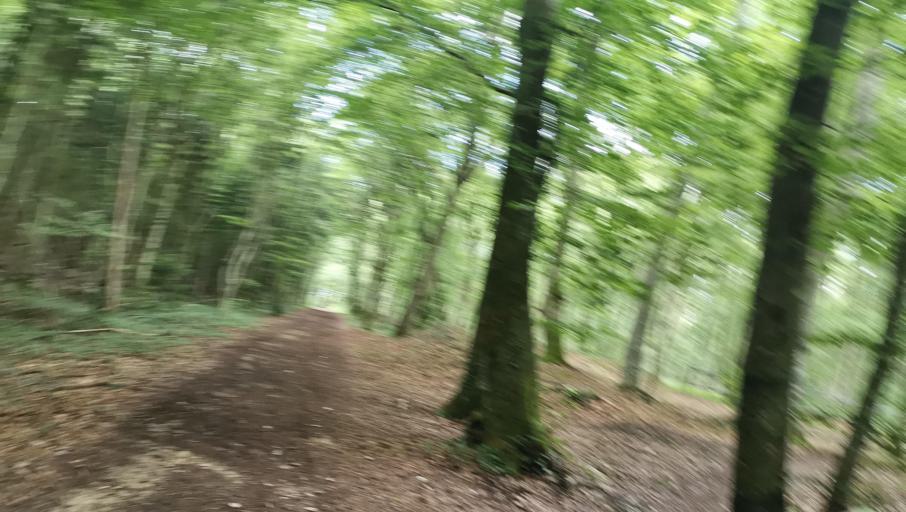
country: FR
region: Lorraine
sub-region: Departement de la Meuse
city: Vigneulles-les-Hattonchatel
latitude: 49.0293
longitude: 5.5842
